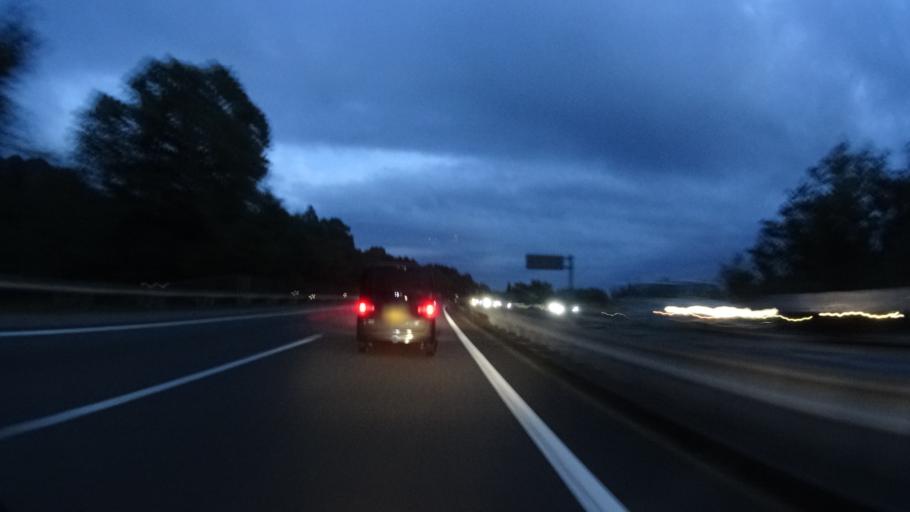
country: JP
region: Shiga Prefecture
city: Youkaichi
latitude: 35.1428
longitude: 136.2808
